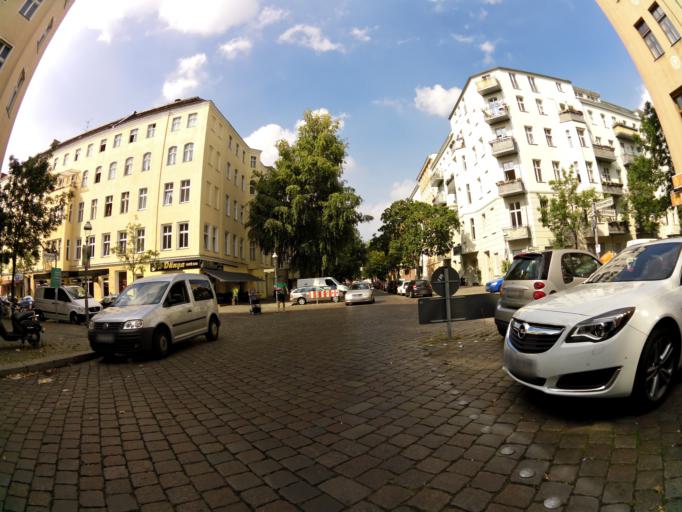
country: DE
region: Berlin
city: Wedding Bezirk
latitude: 52.5427
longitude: 13.3628
